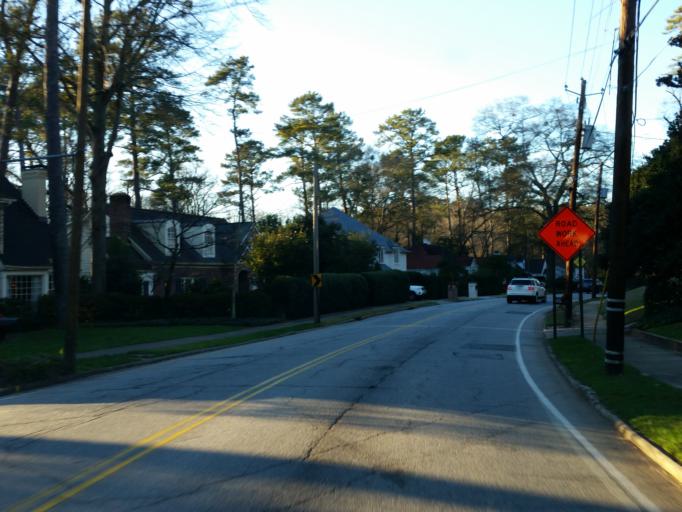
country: US
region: Georgia
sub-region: Cobb County
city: Vinings
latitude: 33.8221
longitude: -84.4056
